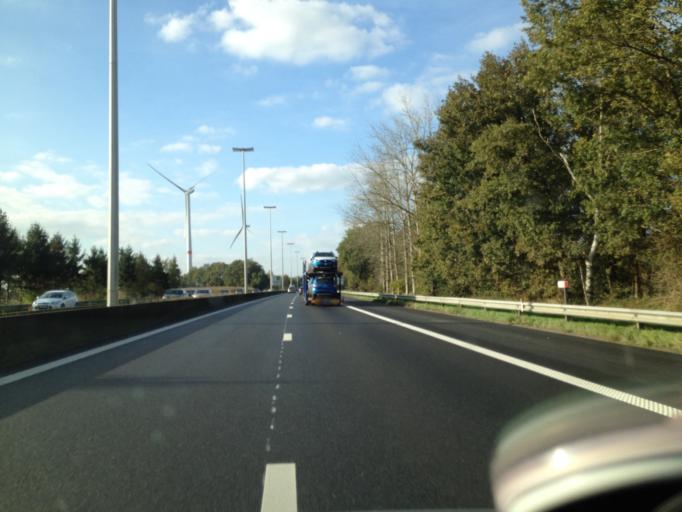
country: BE
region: Flanders
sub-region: Provincie Antwerpen
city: Geel
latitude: 51.1202
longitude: 4.9665
